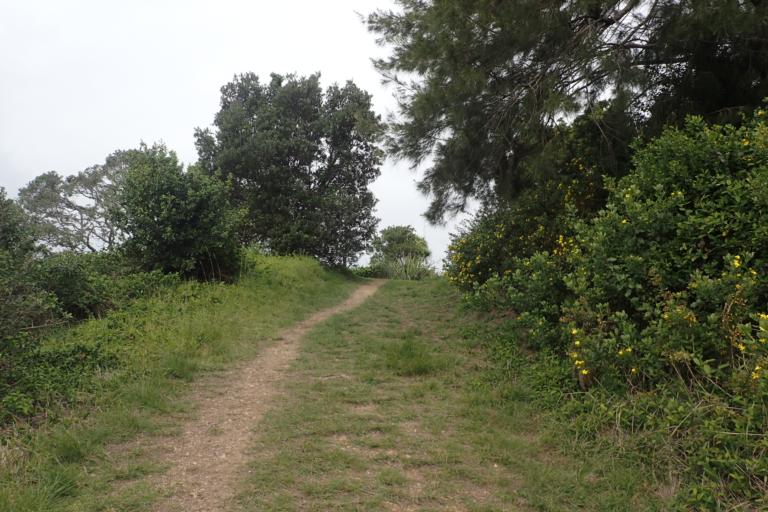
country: NZ
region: Auckland
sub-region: Auckland
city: Pakuranga
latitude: -36.7910
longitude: 175.0073
